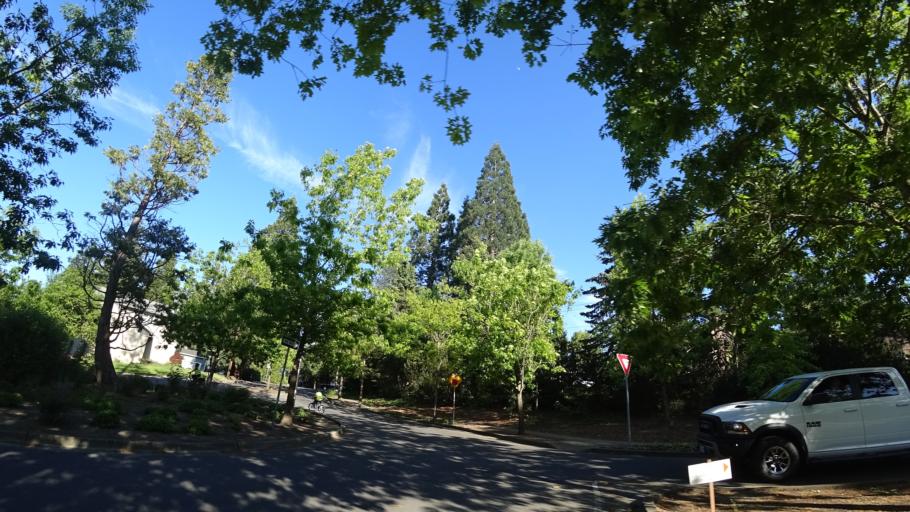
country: US
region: Oregon
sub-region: Washington County
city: Beaverton
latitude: 45.4669
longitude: -122.8090
